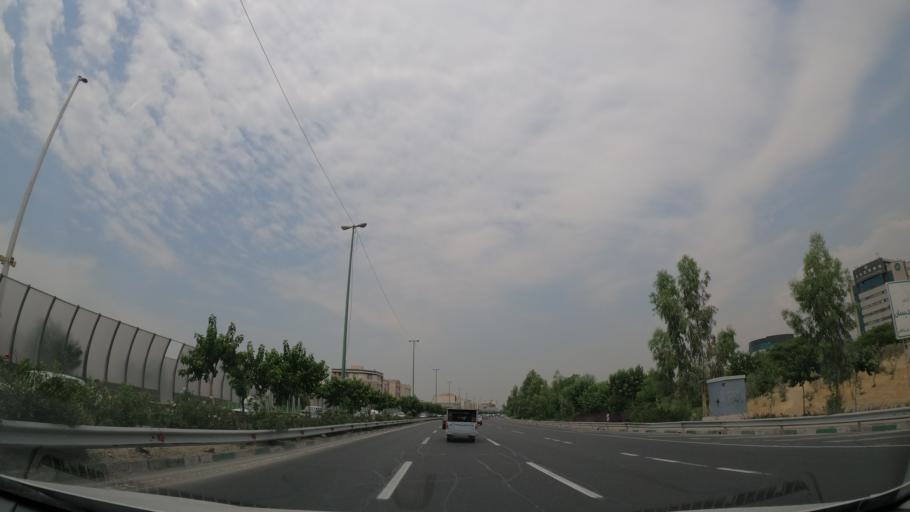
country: IR
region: Tehran
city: Tehran
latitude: 35.7389
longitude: 51.3629
